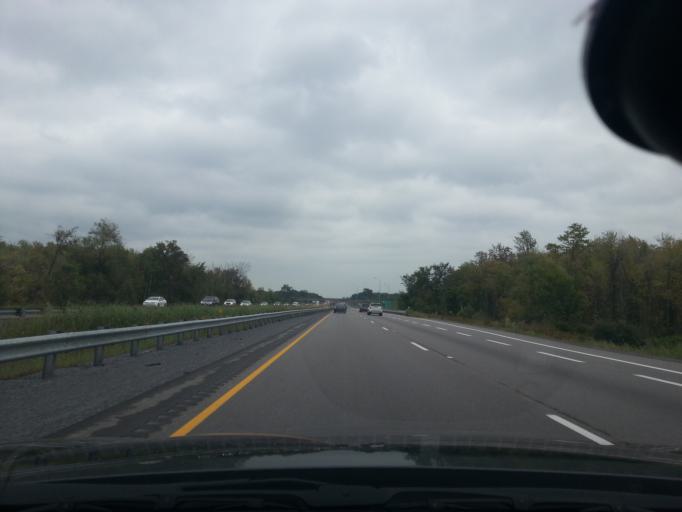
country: CA
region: Ontario
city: Skatepark
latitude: 44.2821
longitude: -76.7227
